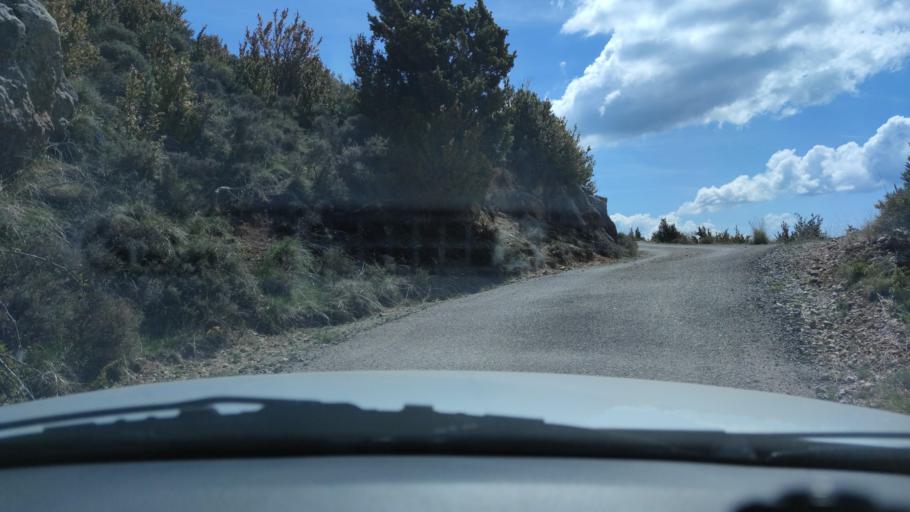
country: ES
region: Catalonia
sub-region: Provincia de Lleida
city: Sort
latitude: 42.2977
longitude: 1.1714
